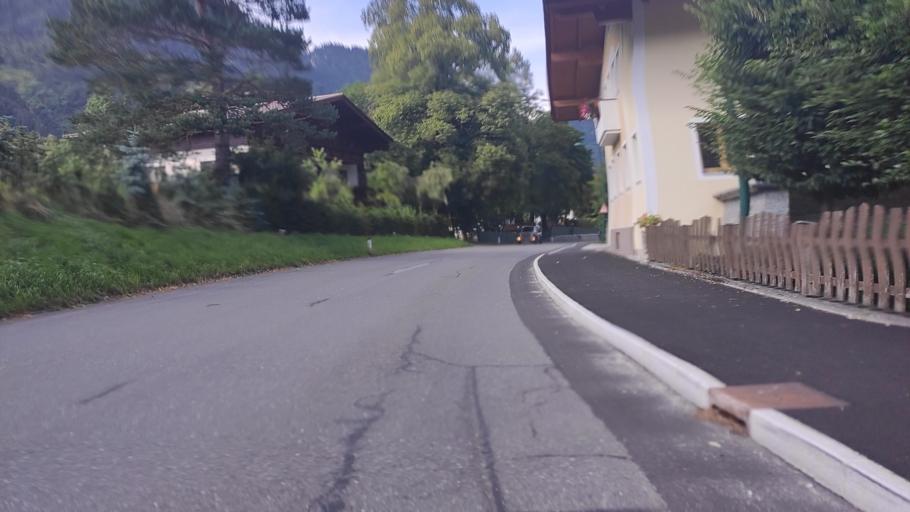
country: AT
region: Salzburg
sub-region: Politischer Bezirk Zell am See
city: Unken
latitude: 47.6532
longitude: 12.7327
